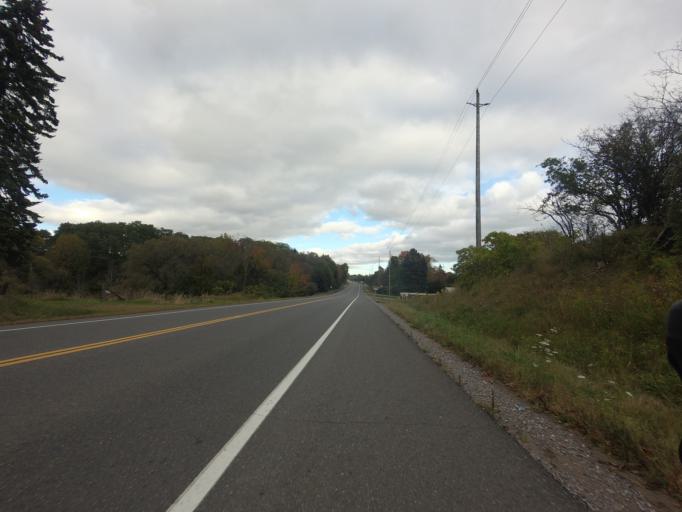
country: CA
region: Ontario
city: Cobourg
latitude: 43.9787
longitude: -78.0851
